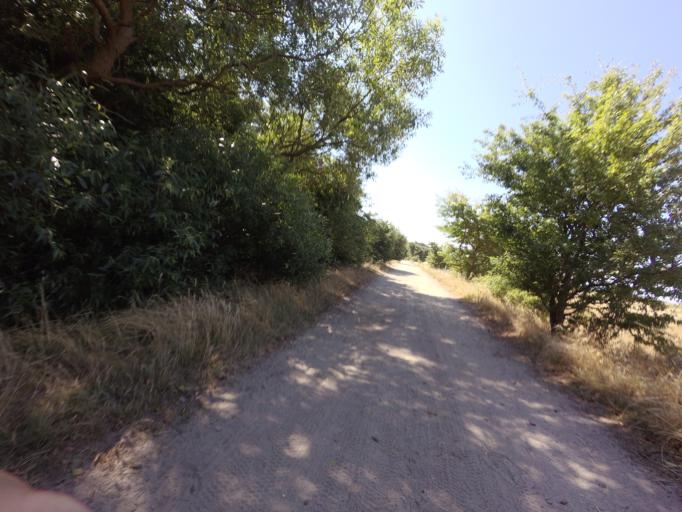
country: SE
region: Skane
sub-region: Vellinge Kommun
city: Skanor med Falsterbo
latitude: 55.3968
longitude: 12.8300
